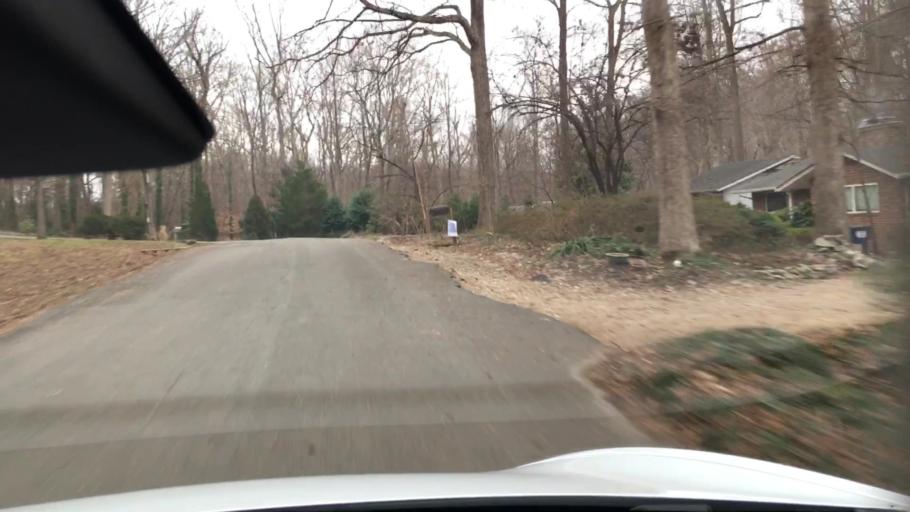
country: US
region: Virginia
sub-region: Chesterfield County
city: Bon Air
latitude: 37.5289
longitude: -77.5653
